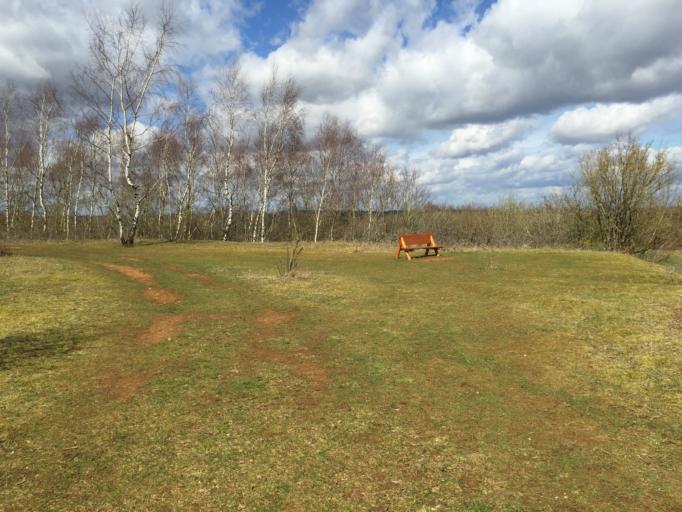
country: LU
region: Luxembourg
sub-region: Canton d'Esch-sur-Alzette
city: Petange
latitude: 49.5459
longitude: 5.8803
